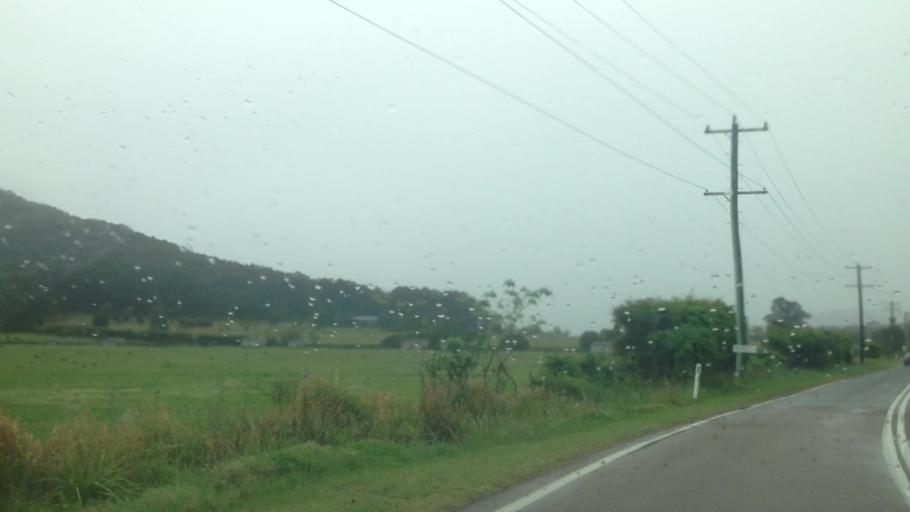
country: AU
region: New South Wales
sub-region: Wyong Shire
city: Little Jilliby
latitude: -33.2346
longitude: 151.3759
